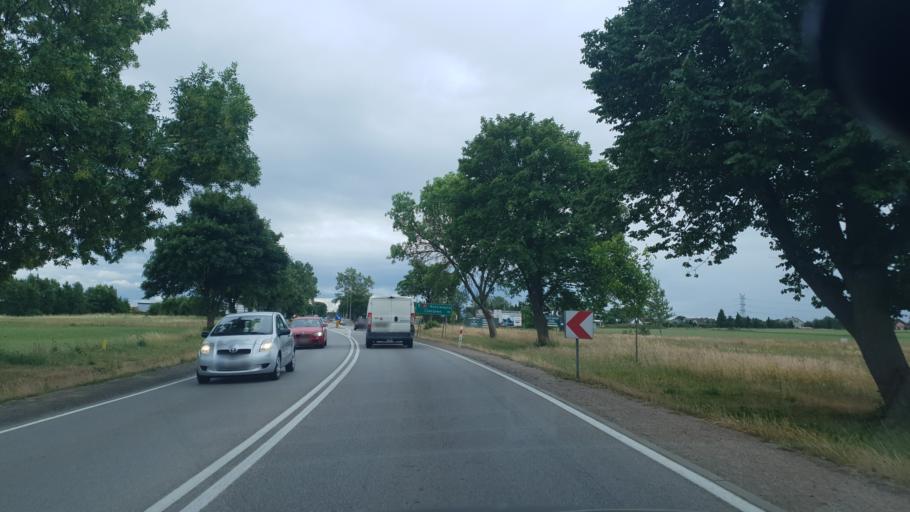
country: PL
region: Pomeranian Voivodeship
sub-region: Powiat kartuski
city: Banino
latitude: 54.3934
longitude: 18.3567
